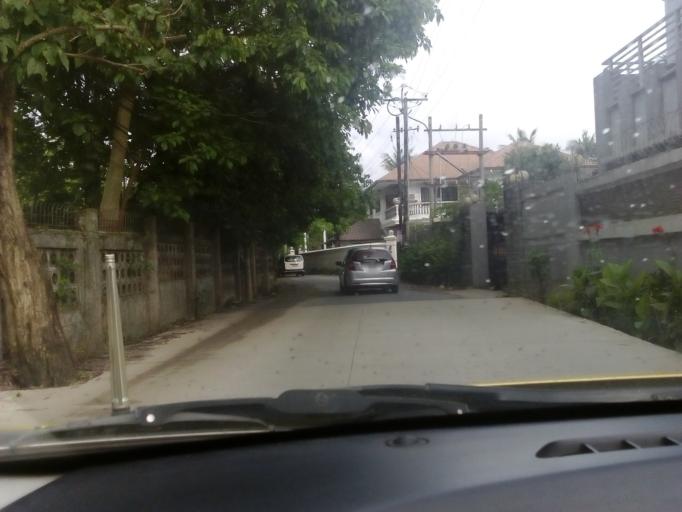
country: MM
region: Yangon
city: Yangon
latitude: 16.8491
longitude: 96.1512
